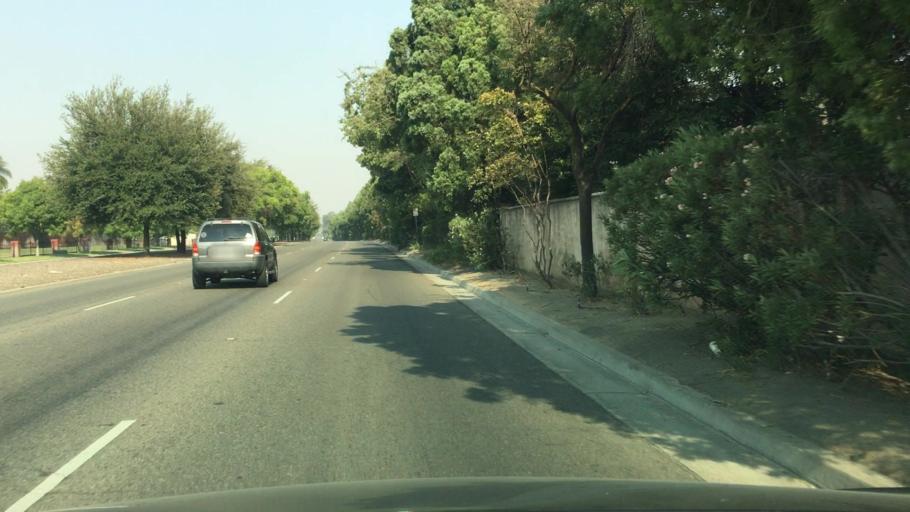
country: US
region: California
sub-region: Fresno County
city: Fresno
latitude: 36.8371
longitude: -119.8461
